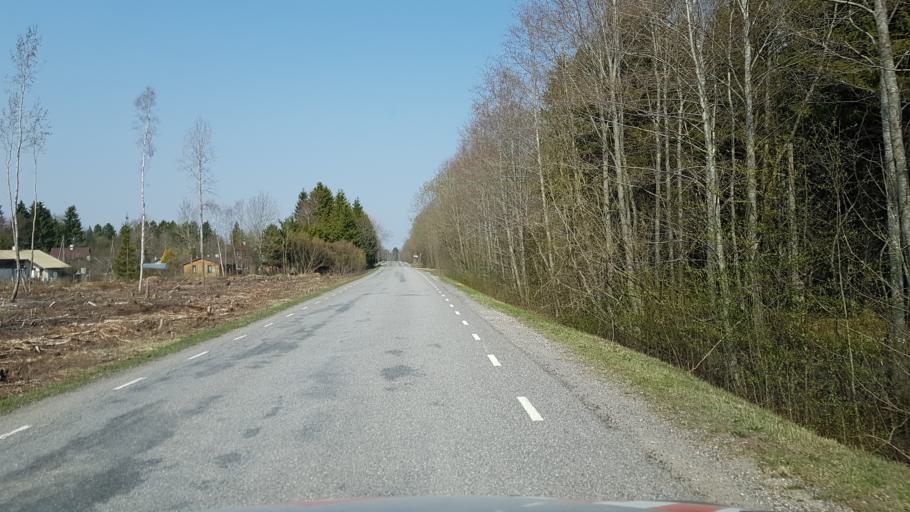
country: EE
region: Raplamaa
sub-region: Kohila vald
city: Kohila
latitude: 59.2034
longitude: 24.6678
